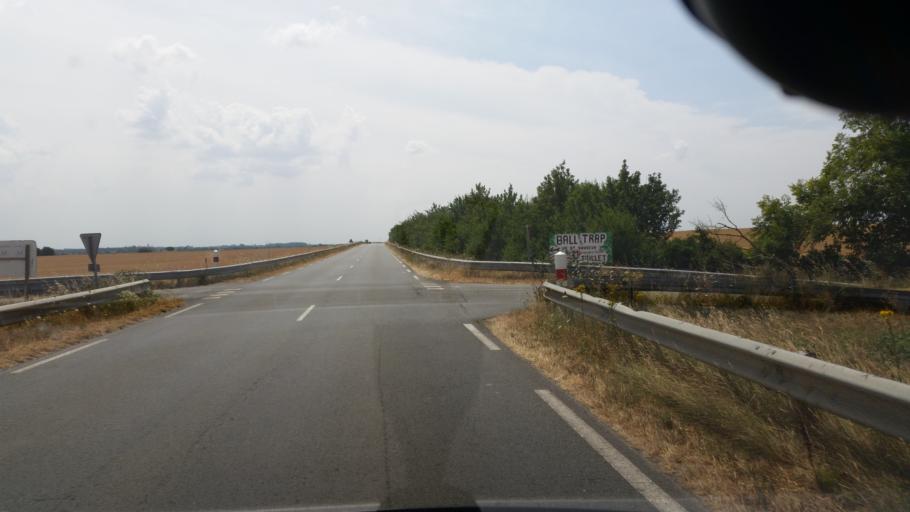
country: FR
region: Poitou-Charentes
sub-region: Departement de la Charente-Maritime
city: Saint-Jean-de-Liversay
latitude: 46.2053
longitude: -0.8739
